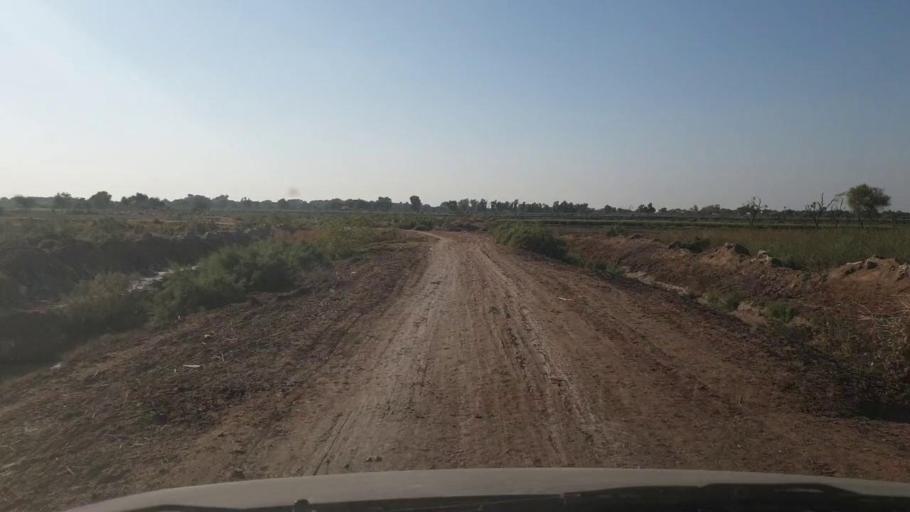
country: PK
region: Sindh
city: Mirwah Gorchani
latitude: 25.3611
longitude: 69.0913
